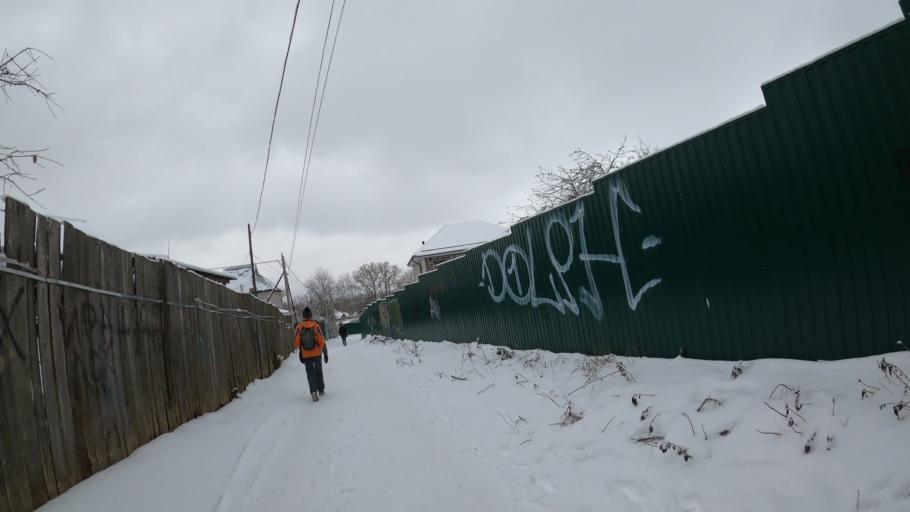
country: RU
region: Jaroslavl
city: Pereslavl'-Zalesskiy
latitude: 56.7458
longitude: 38.8634
